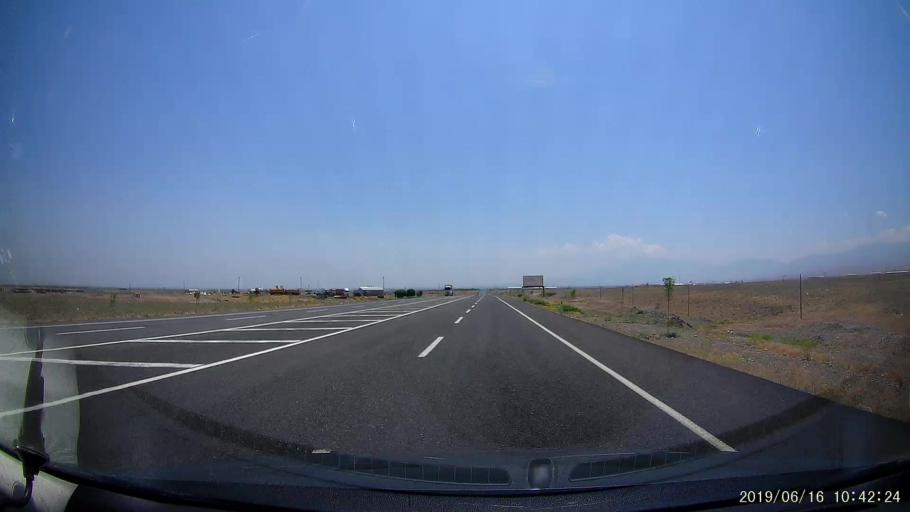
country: AM
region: Armavir
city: Shenavan
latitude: 40.0423
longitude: 43.8057
